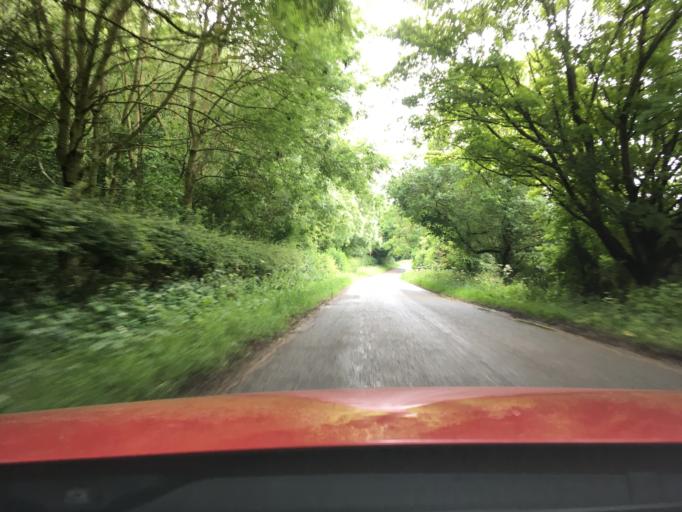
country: GB
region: England
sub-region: Gloucestershire
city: Mickleton
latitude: 52.0828
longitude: -1.7155
